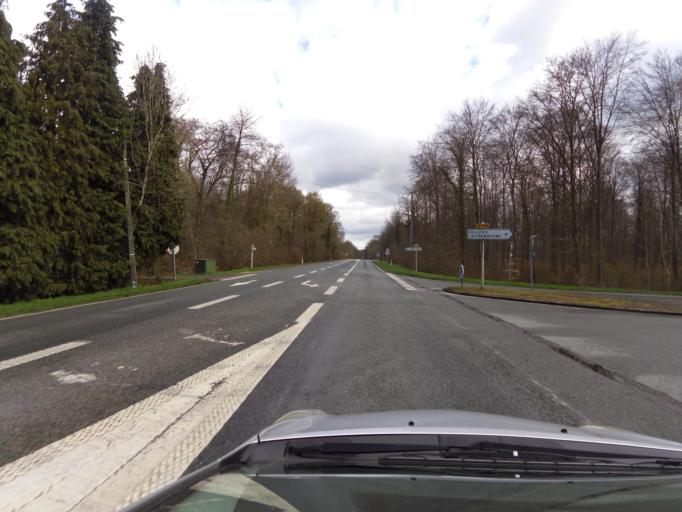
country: FR
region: Picardie
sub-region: Departement de l'Oise
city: Pont-Sainte-Maxence
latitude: 49.2826
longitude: 2.5991
